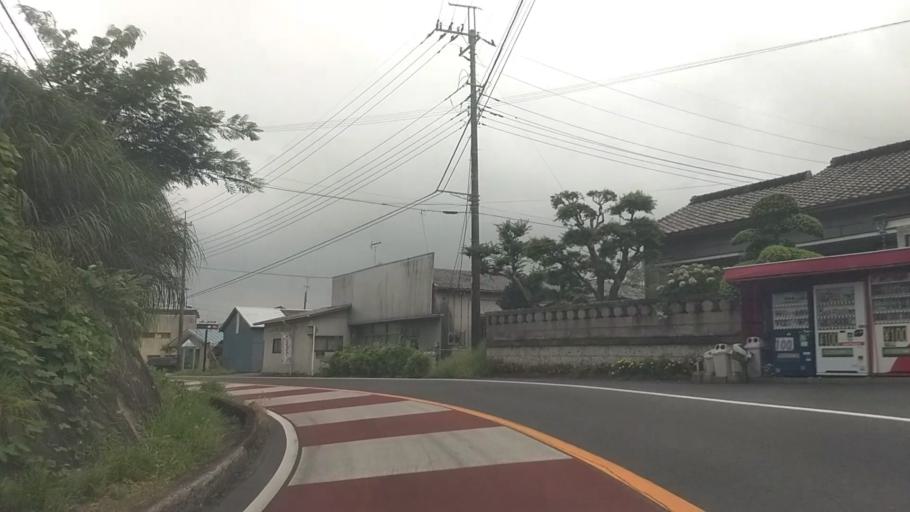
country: JP
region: Chiba
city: Katsuura
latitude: 35.2413
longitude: 140.2384
